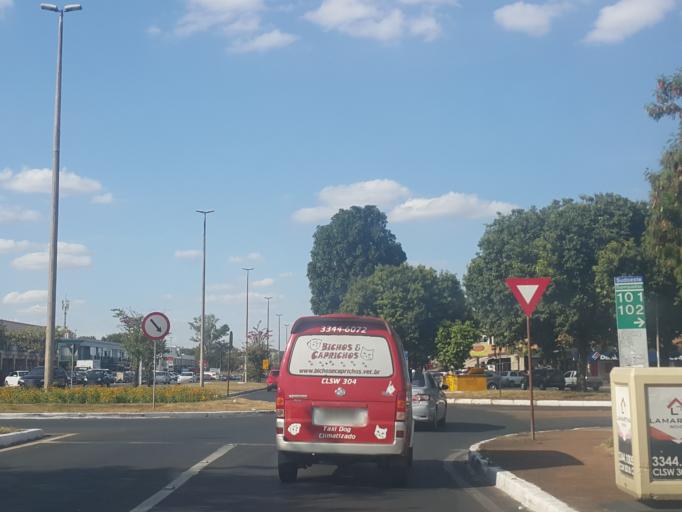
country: BR
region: Federal District
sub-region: Brasilia
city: Brasilia
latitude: -15.7990
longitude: -47.9219
